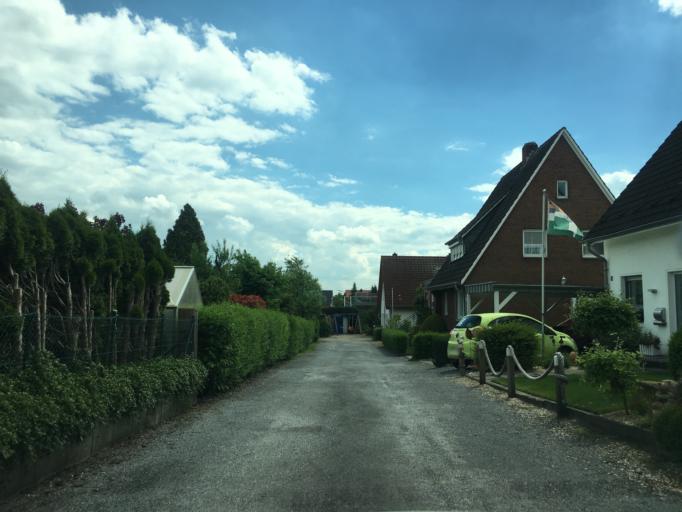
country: DE
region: North Rhine-Westphalia
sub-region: Regierungsbezirk Munster
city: Altenberge
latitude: 52.0437
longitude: 7.4722
